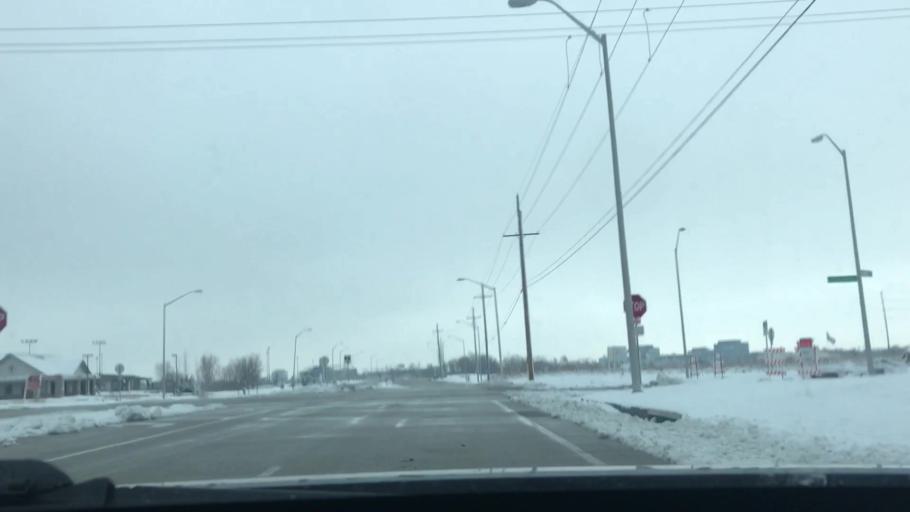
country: US
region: Missouri
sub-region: Platte County
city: Weatherby Lake
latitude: 39.2610
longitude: -94.6681
